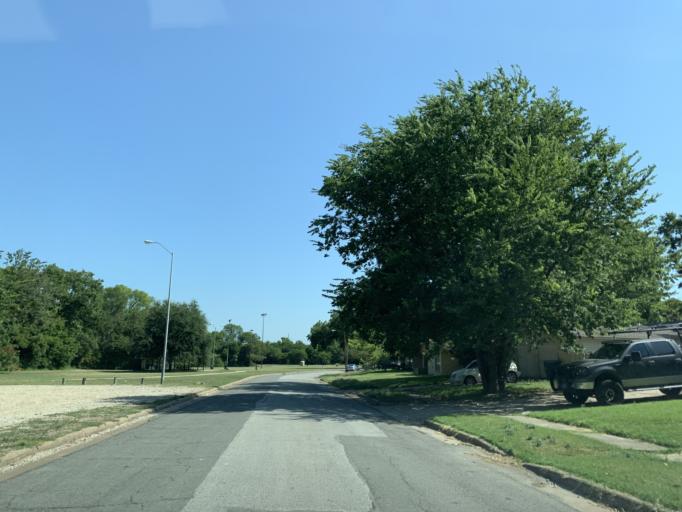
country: US
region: Texas
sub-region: Dallas County
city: Hutchins
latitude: 32.6711
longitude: -96.7483
